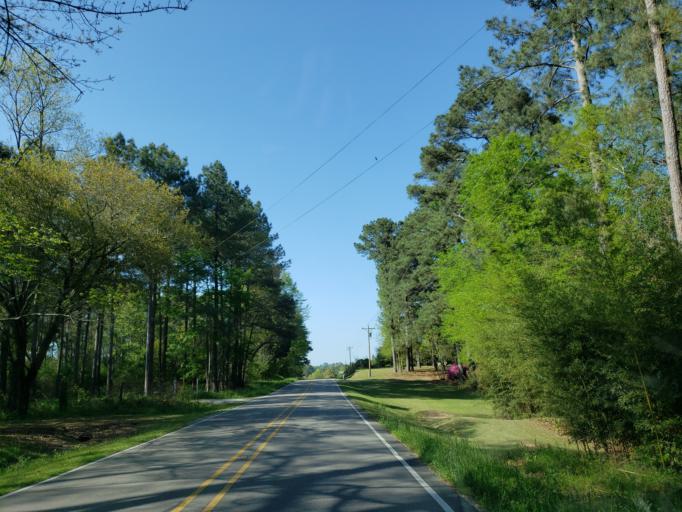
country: US
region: Mississippi
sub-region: Forrest County
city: Rawls Springs
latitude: 31.5456
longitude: -89.3652
